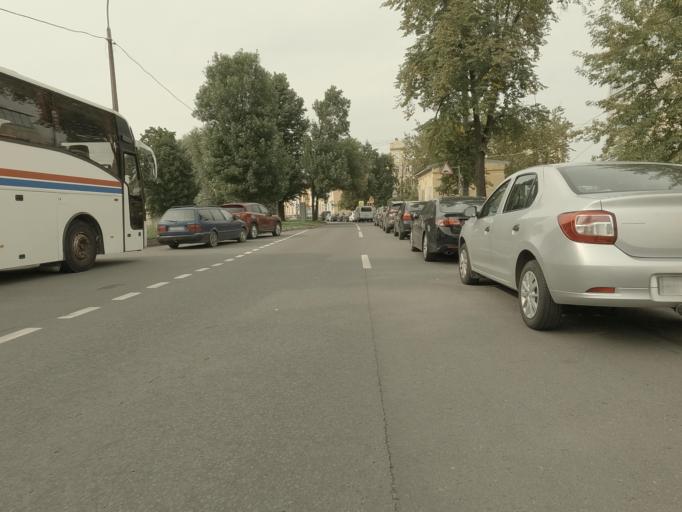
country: RU
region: St.-Petersburg
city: Admiralteisky
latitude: 59.9110
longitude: 30.2879
